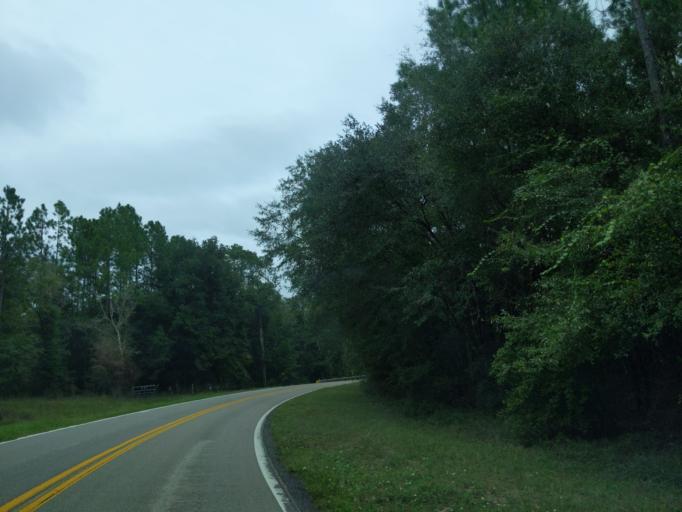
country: US
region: Florida
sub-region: Gadsden County
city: Midway
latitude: 30.4182
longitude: -84.4181
